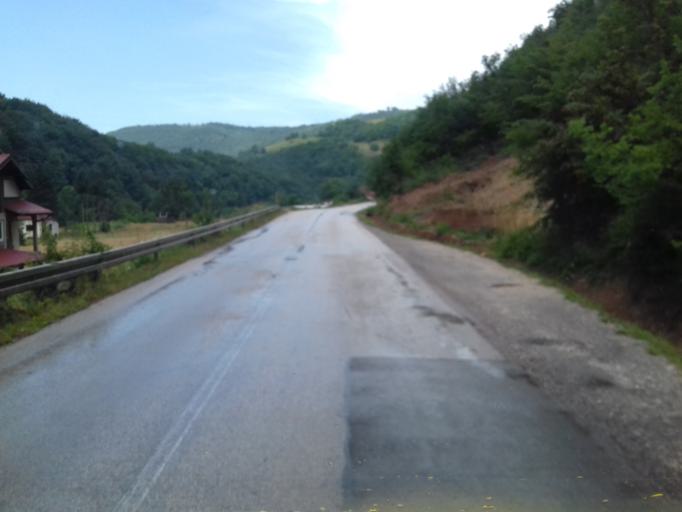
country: BA
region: Federation of Bosnia and Herzegovina
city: Kiseljak
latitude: 43.9529
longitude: 18.1291
